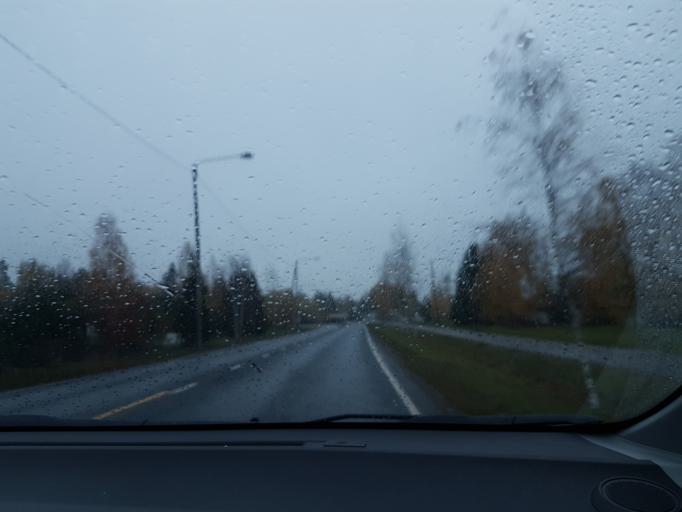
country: FI
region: Uusimaa
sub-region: Helsinki
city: Jaervenpaeae
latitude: 60.5420
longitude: 25.1160
